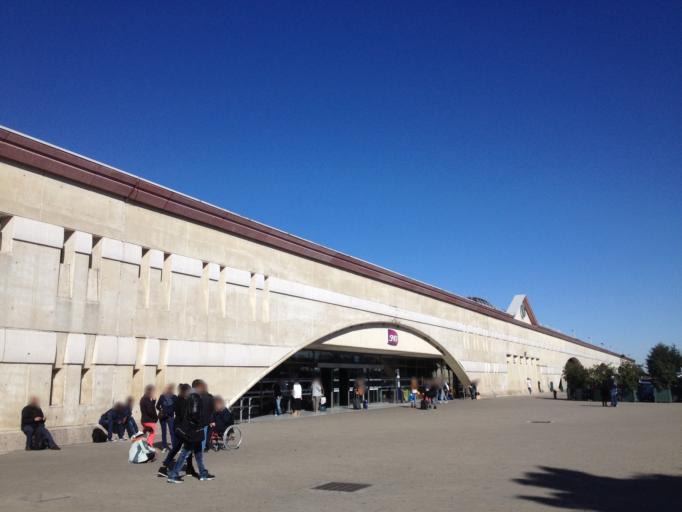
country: FR
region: Ile-de-France
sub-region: Departement de Seine-et-Marne
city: Chessy
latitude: 48.8700
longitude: 2.7833
